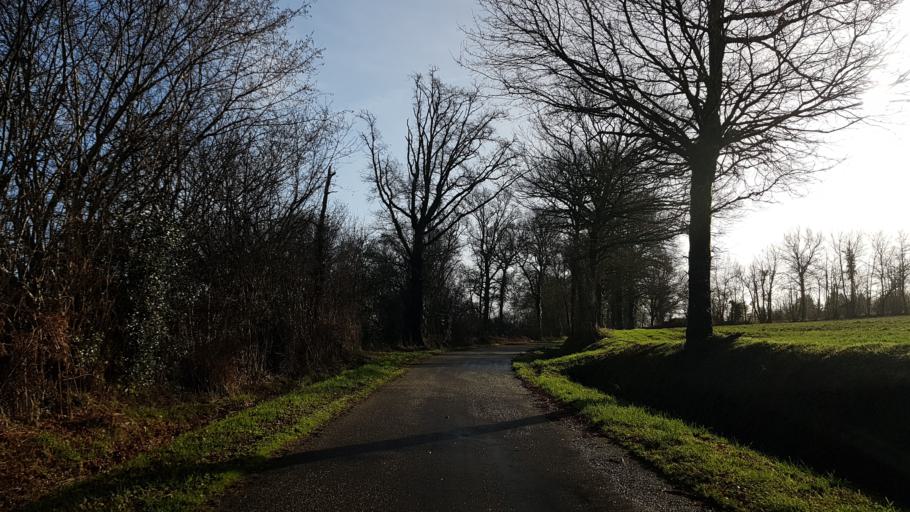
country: FR
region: Poitou-Charentes
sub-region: Departement de la Charente
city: Etagnac
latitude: 45.9229
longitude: 0.8175
